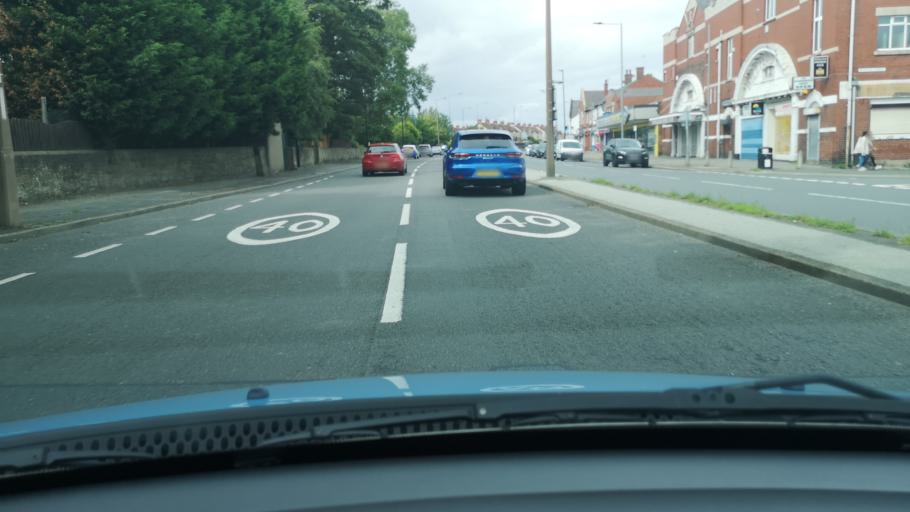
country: GB
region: England
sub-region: Doncaster
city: Carcroft
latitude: 53.5616
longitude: -1.1933
